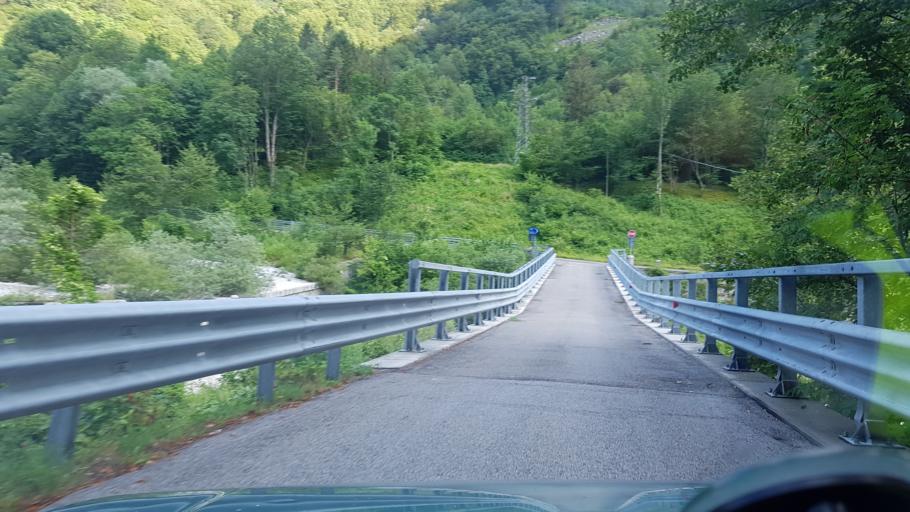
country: IT
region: Friuli Venezia Giulia
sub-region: Provincia di Udine
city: Lusevera
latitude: 46.3081
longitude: 13.2738
